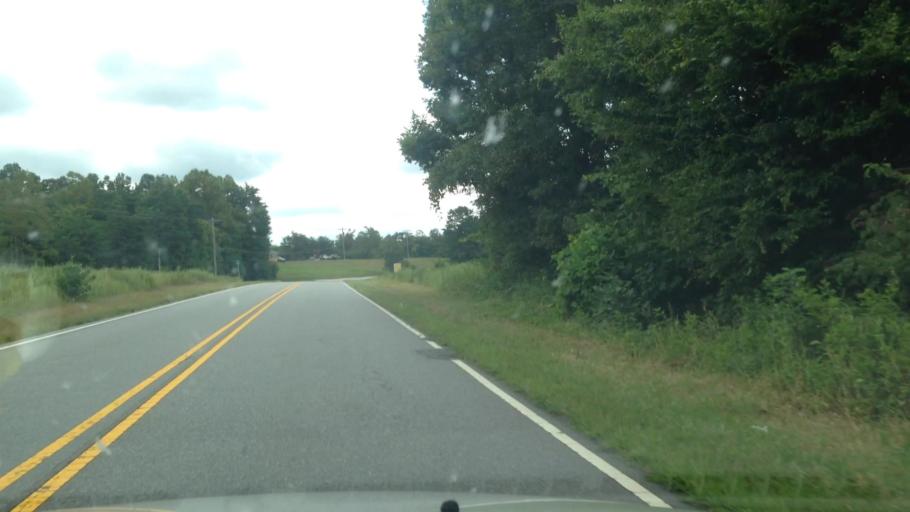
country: US
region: North Carolina
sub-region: Rockingham County
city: Mayodan
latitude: 36.4203
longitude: -80.0710
